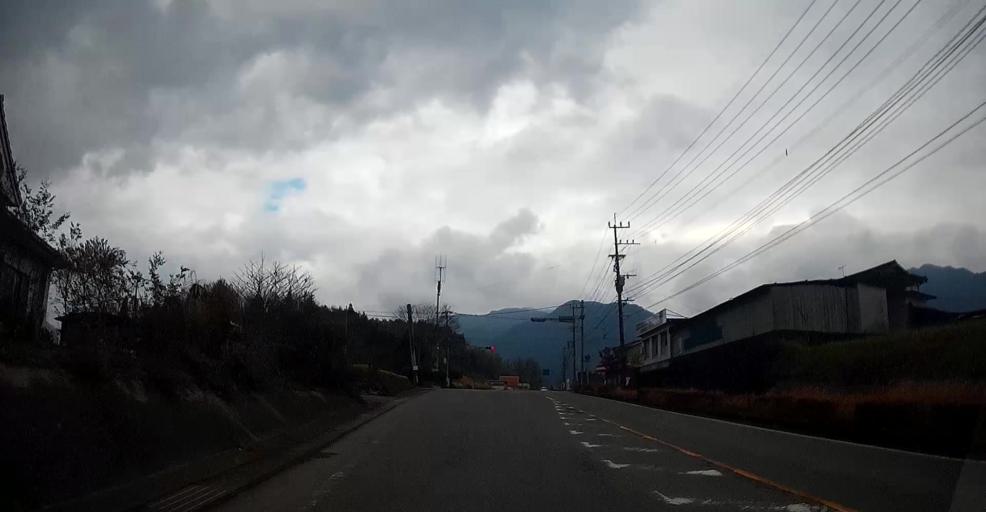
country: JP
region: Kumamoto
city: Matsubase
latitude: 32.6202
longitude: 130.8341
